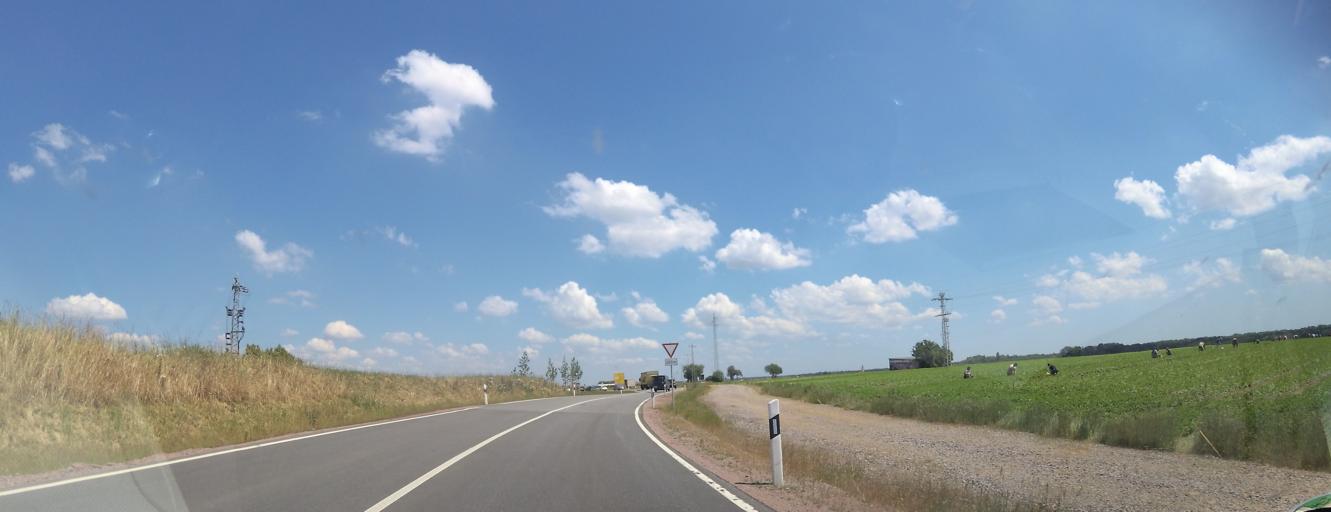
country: DE
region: Rheinland-Pfalz
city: Hochstadt
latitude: 49.2392
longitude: 8.2204
